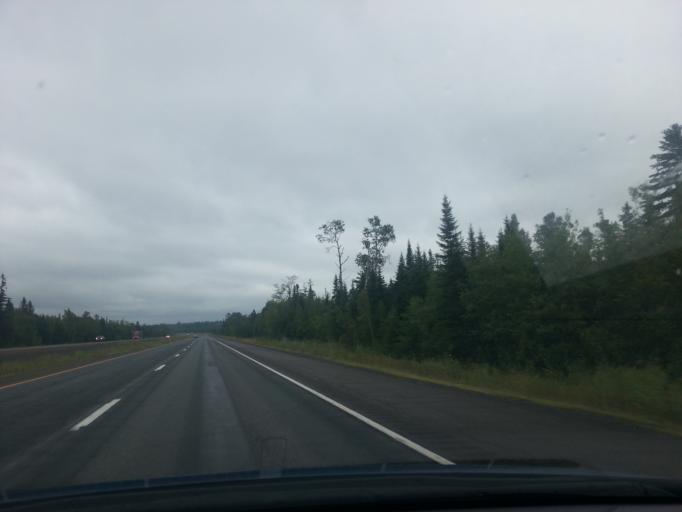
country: CA
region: New Brunswick
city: Fredericton
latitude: 45.8907
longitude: -66.6447
